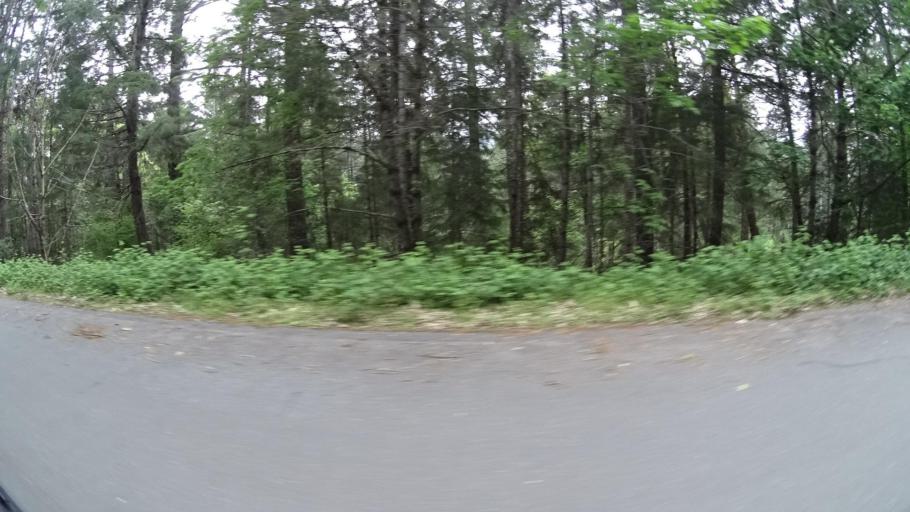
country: US
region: California
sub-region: Humboldt County
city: Willow Creek
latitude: 41.1182
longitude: -123.7353
